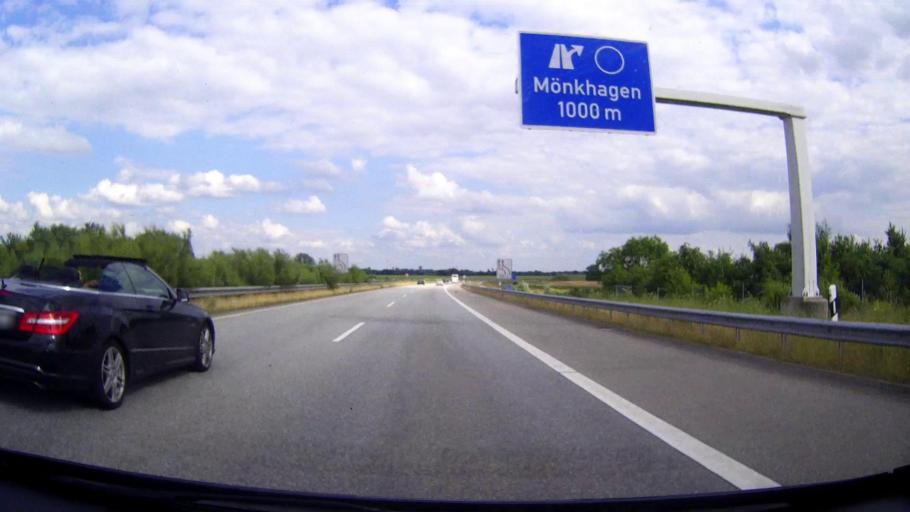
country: DE
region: Schleswig-Holstein
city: Monkhagen
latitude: 53.9100
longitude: 10.5561
